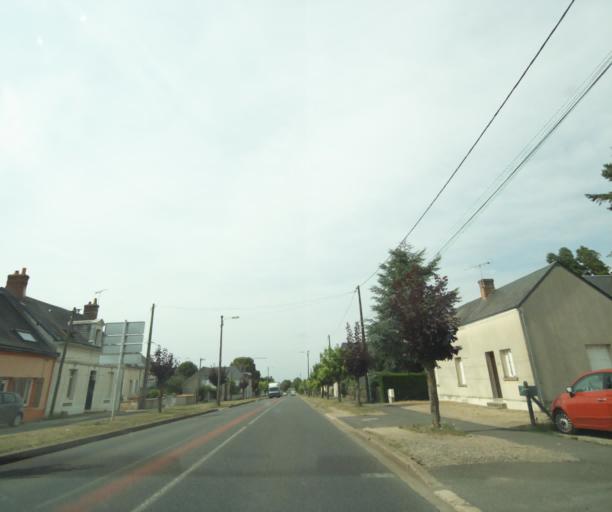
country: FR
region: Centre
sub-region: Departement d'Indre-et-Loire
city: Neuille-Pont-Pierre
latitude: 47.5486
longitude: 0.5509
